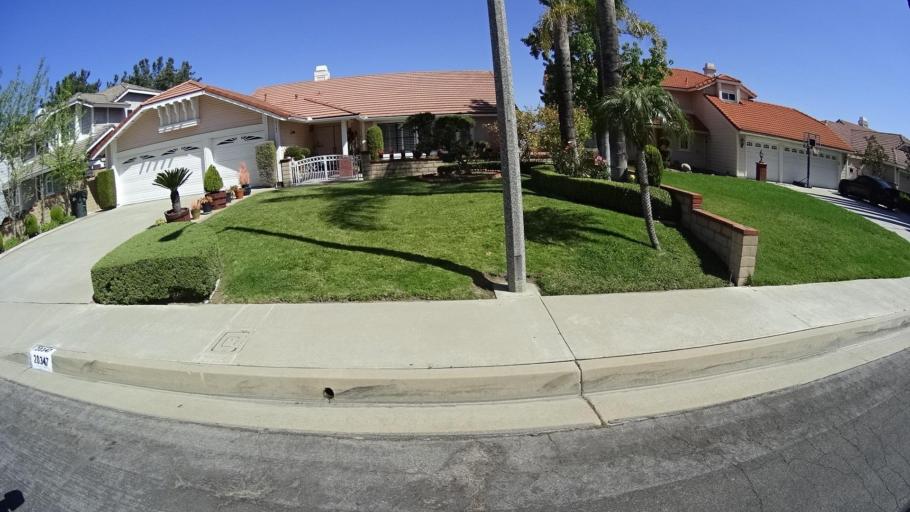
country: US
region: California
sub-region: Los Angeles County
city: Rowland Heights
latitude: 33.9738
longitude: -117.8596
